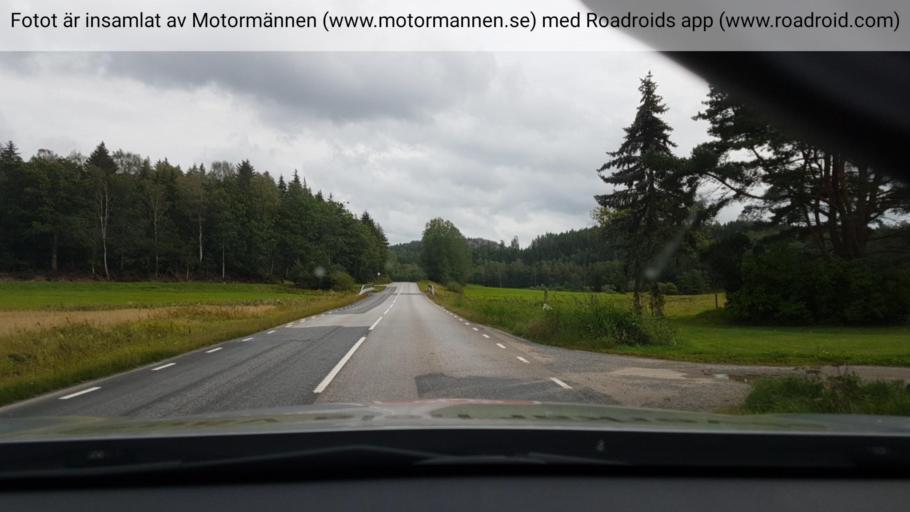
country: SE
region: Vaestra Goetaland
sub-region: Sotenas Kommun
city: Hunnebostrand
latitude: 58.5512
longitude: 11.4105
